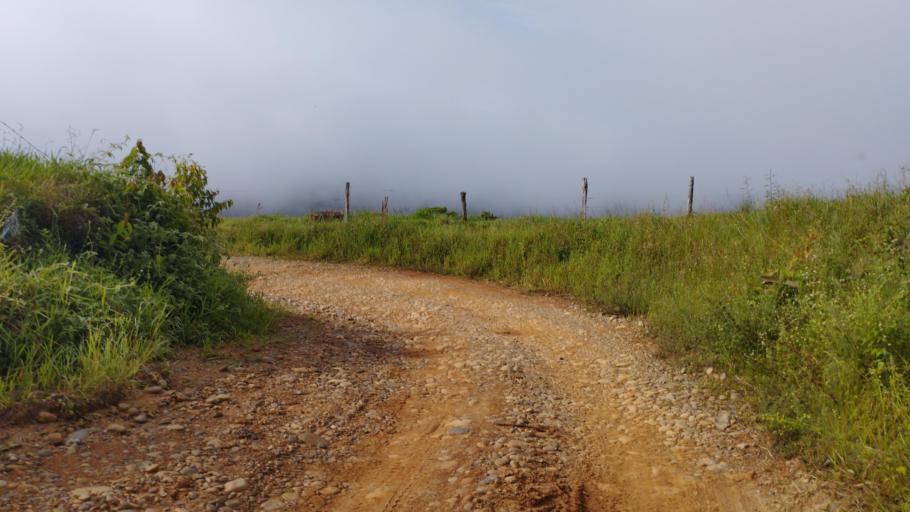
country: CO
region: Casanare
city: Sabanalarga
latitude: 4.7662
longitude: -73.0799
